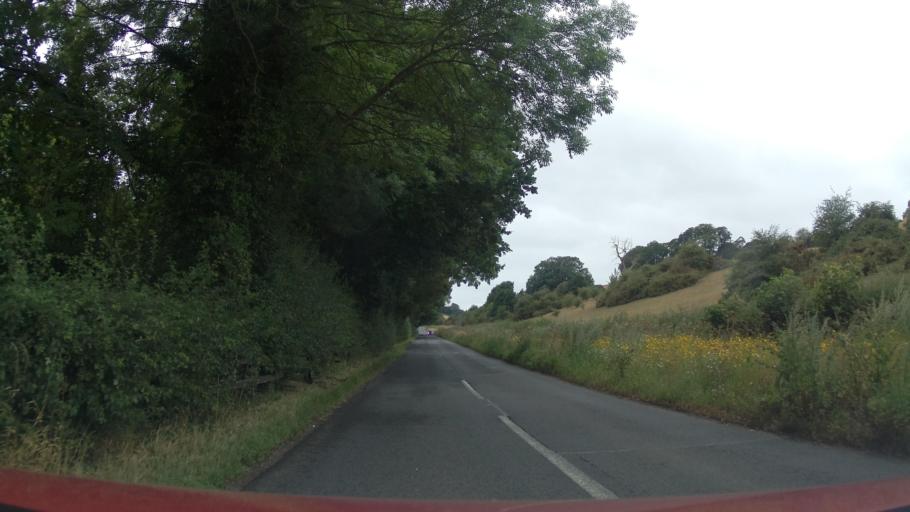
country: GB
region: England
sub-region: Derbyshire
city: Repton
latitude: 52.8227
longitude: -1.5384
